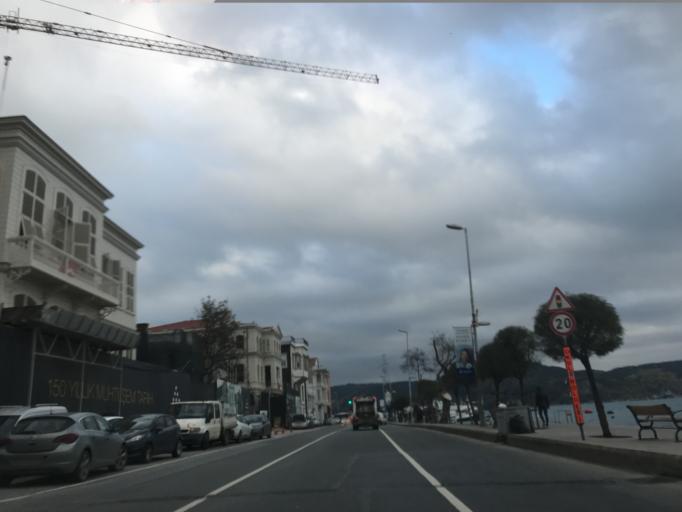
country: TR
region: Istanbul
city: Arikoey
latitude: 41.1652
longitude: 29.0537
